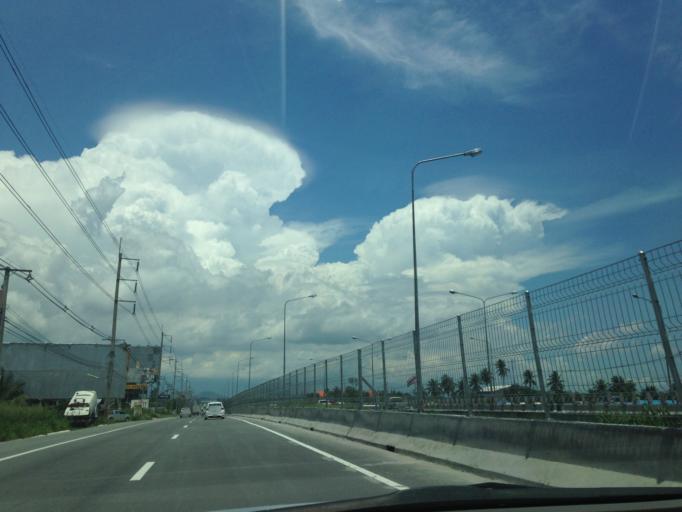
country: TH
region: Chon Buri
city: Si Racha
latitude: 13.2517
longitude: 100.9932
